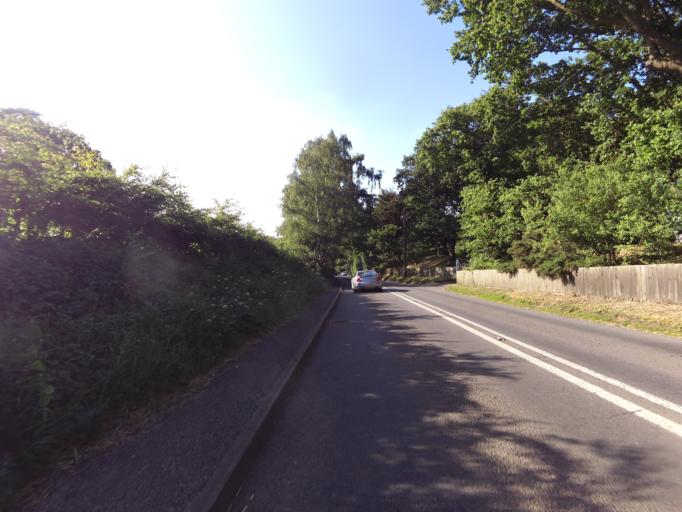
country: GB
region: England
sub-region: Suffolk
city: Woodbridge
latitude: 52.0982
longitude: 1.3483
